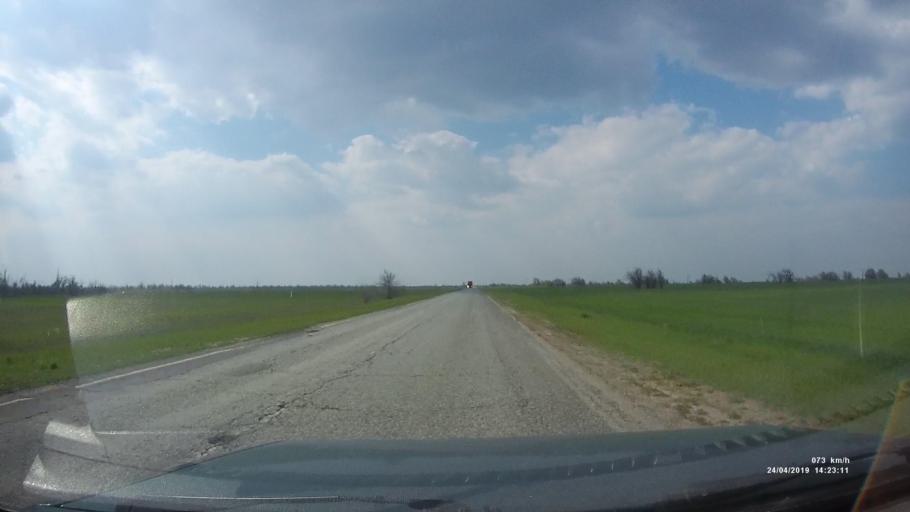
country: RU
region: Kalmykiya
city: Arshan'
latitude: 46.3199
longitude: 44.1178
